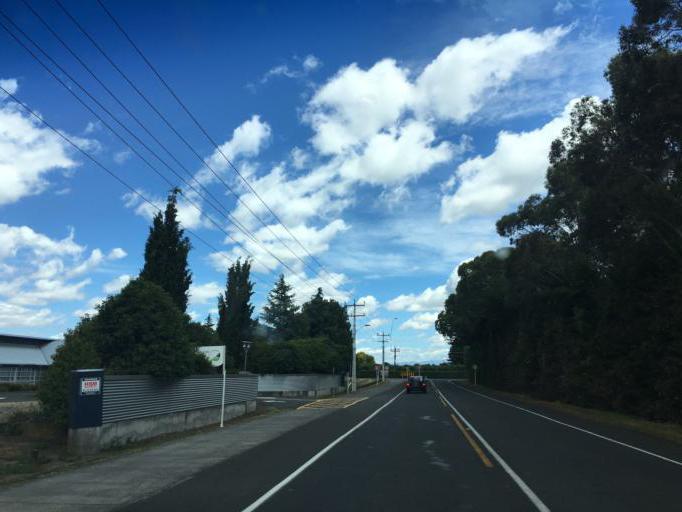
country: NZ
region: Hawke's Bay
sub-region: Hastings District
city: Hastings
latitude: -39.6538
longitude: 176.8769
